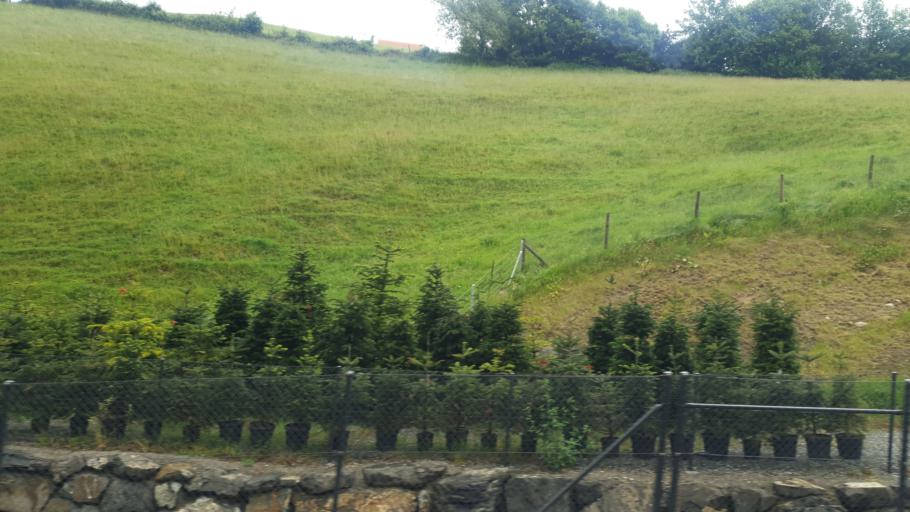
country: CH
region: Appenzell Ausserrhoden
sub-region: Bezirk Mittelland
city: Teufen
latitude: 47.3988
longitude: 9.3625
